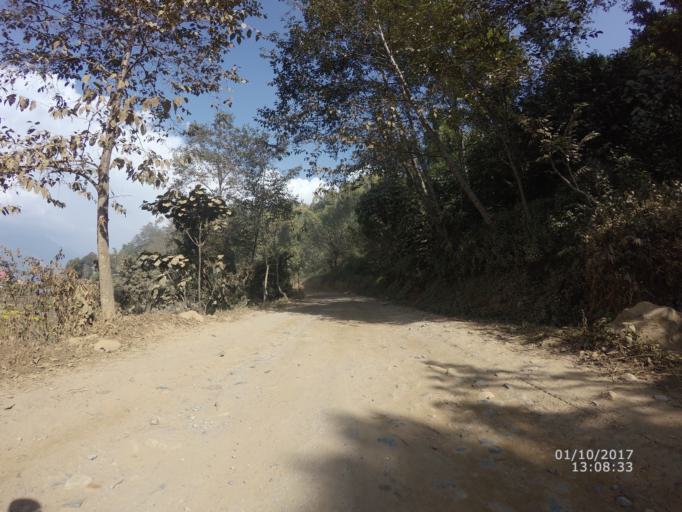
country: NP
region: Western Region
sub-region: Gandaki Zone
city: Pokhara
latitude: 28.3079
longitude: 83.9591
